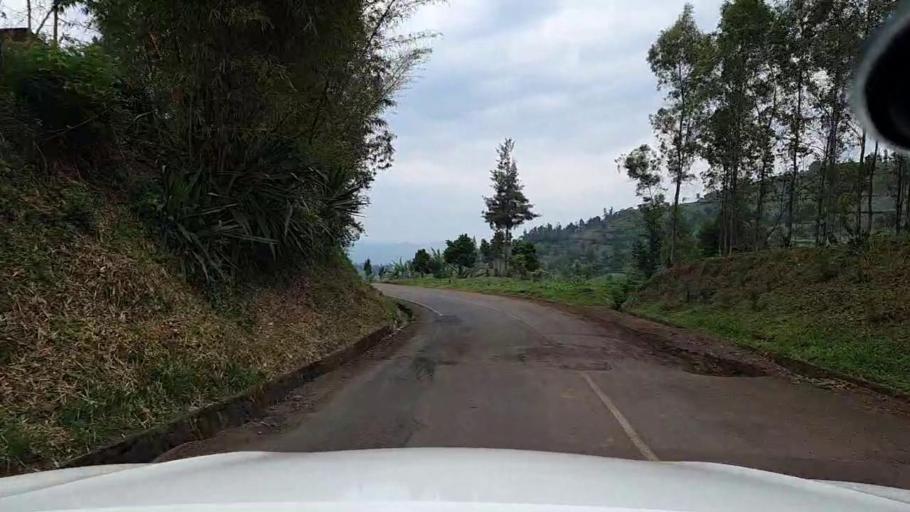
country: RW
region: Western Province
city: Cyangugu
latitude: -2.6589
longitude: 28.9726
